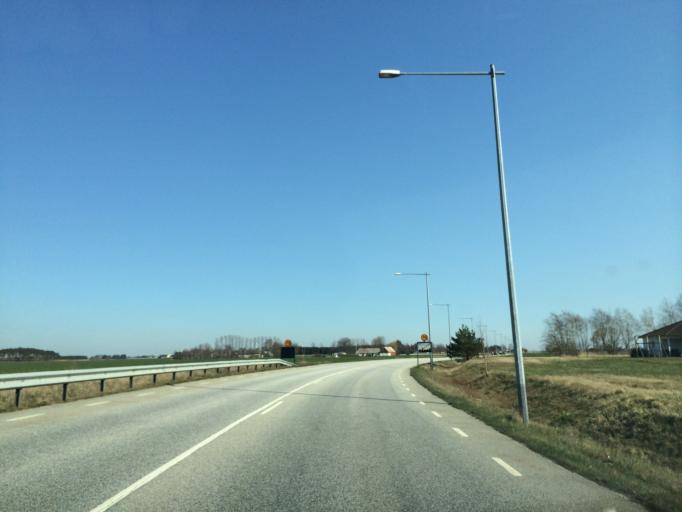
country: SE
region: Skane
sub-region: Kavlinge Kommun
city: Loddekopinge
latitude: 55.7745
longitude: 12.9988
